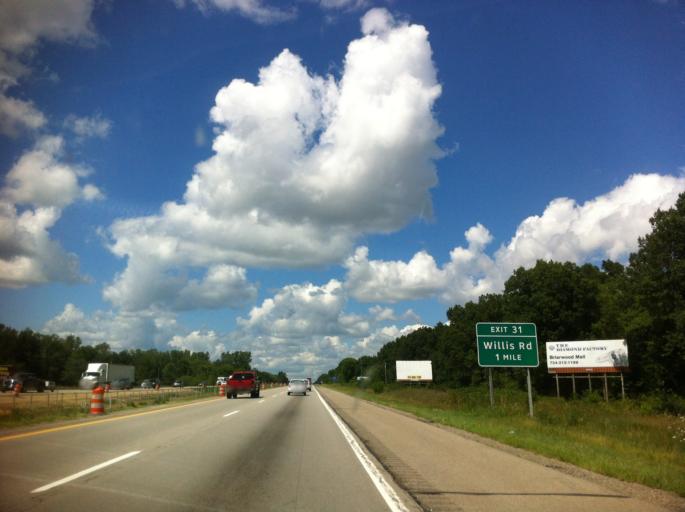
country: US
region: Michigan
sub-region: Washtenaw County
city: Milan
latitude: 42.1371
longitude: -83.6831
